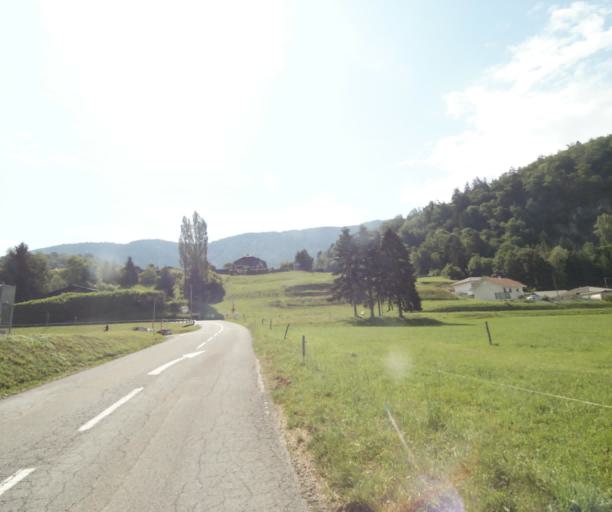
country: FR
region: Rhone-Alpes
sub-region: Departement de la Haute-Savoie
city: Lyaud
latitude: 46.3361
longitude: 6.5159
